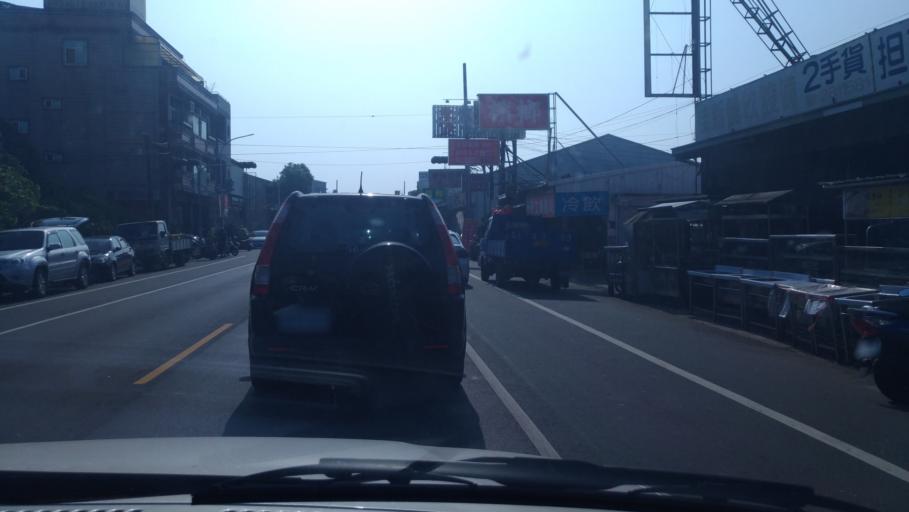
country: TW
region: Taiwan
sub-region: Chiayi
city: Jiayi Shi
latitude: 23.5046
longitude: 120.4381
